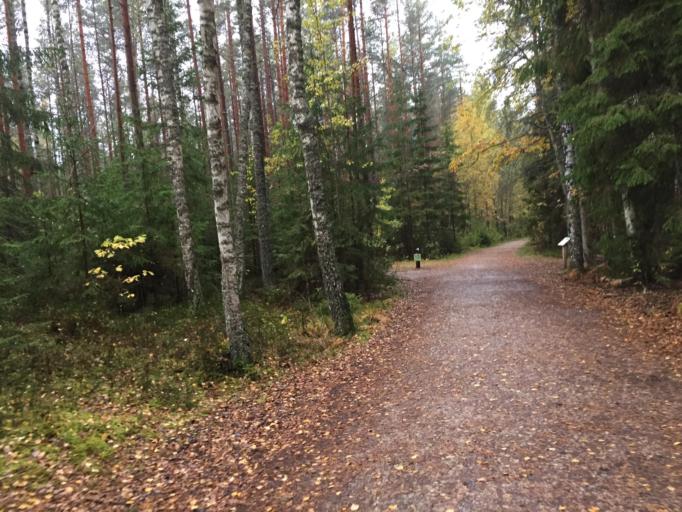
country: LV
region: Engure
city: Smarde
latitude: 56.9127
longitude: 23.4595
